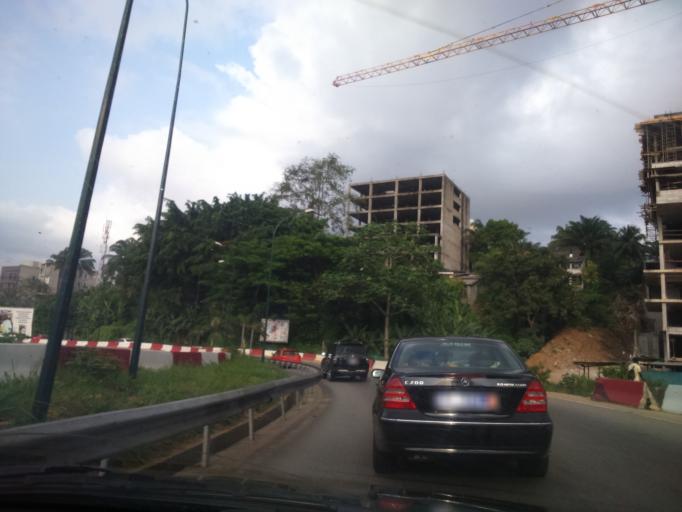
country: CI
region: Lagunes
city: Abidjan
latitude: 5.3378
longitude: -4.0108
